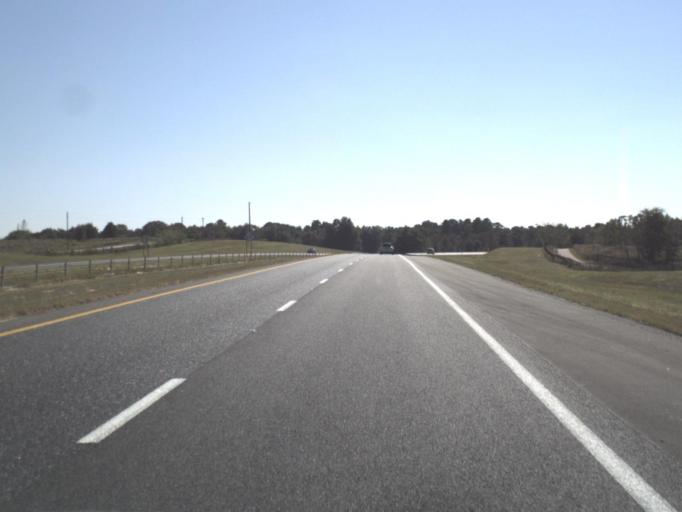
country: US
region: Florida
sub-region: Hernando County
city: Brookridge
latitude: 28.5883
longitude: -82.4825
